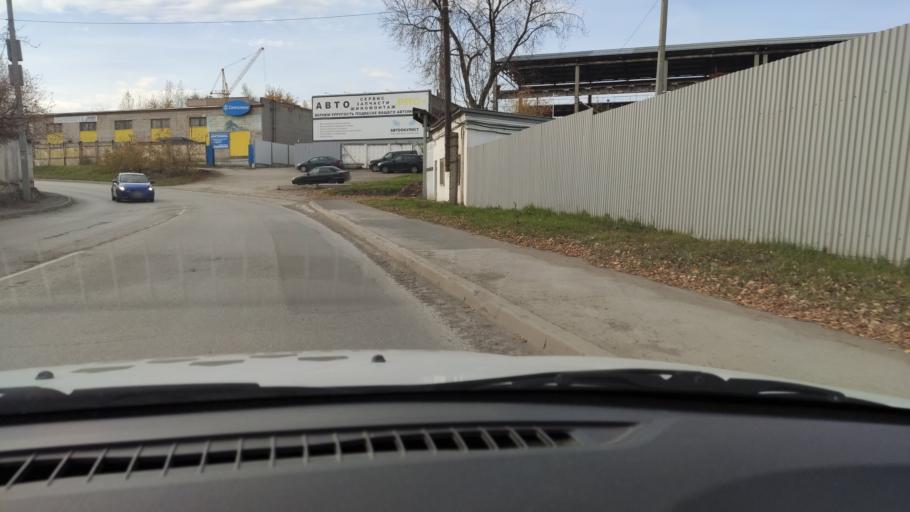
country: RU
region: Perm
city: Perm
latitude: 57.9825
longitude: 56.2719
